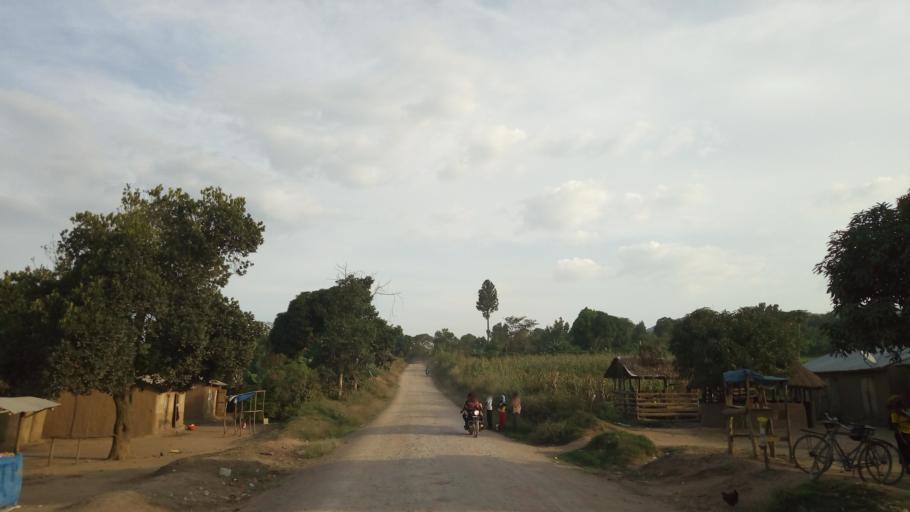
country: UG
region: Central Region
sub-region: Kiboga District
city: Kiboga
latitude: 0.7046
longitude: 31.7781
